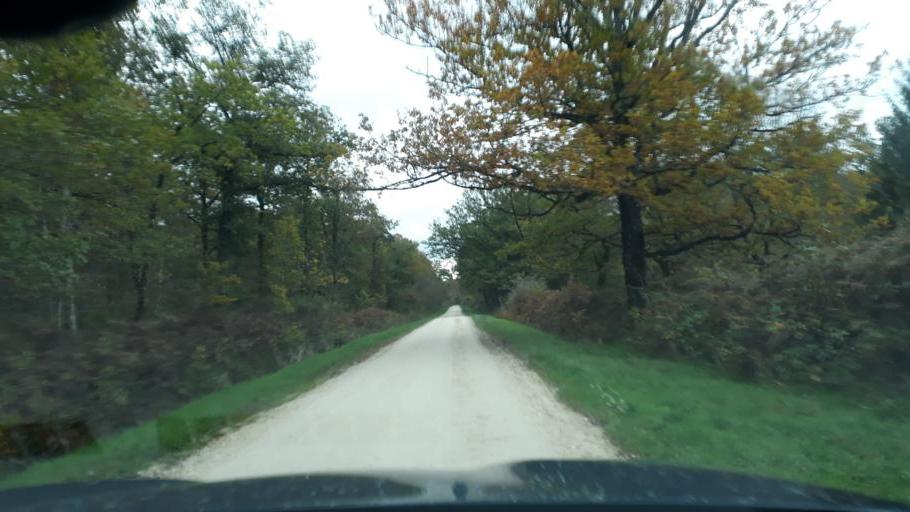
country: FR
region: Centre
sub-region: Departement du Loiret
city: Bouzy-la-Foret
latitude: 47.8194
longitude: 2.4150
